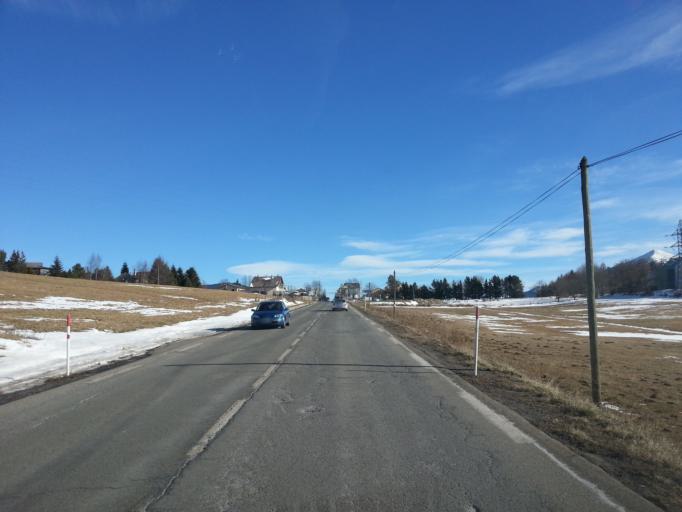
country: ES
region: Catalonia
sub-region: Provincia de Girona
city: Llivia
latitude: 42.4956
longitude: 2.0890
